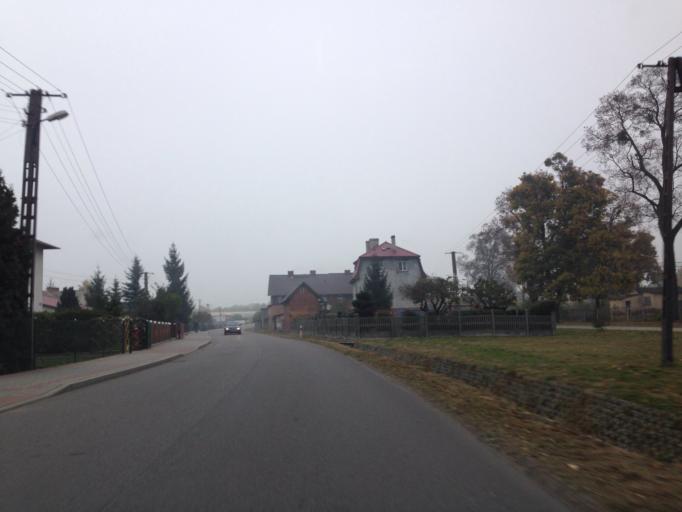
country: PL
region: Warmian-Masurian Voivodeship
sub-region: Powiat nowomiejski
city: Biskupiec
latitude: 53.4909
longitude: 19.3894
